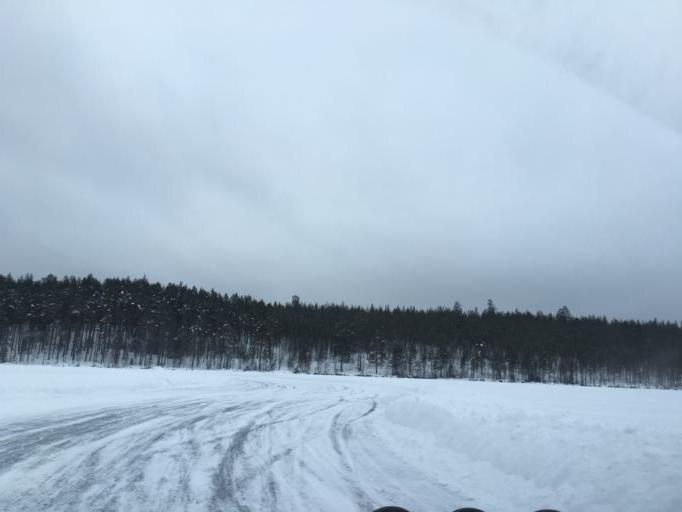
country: SE
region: Dalarna
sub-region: Alvdalens Kommun
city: AElvdalen
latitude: 61.2582
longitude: 14.0963
